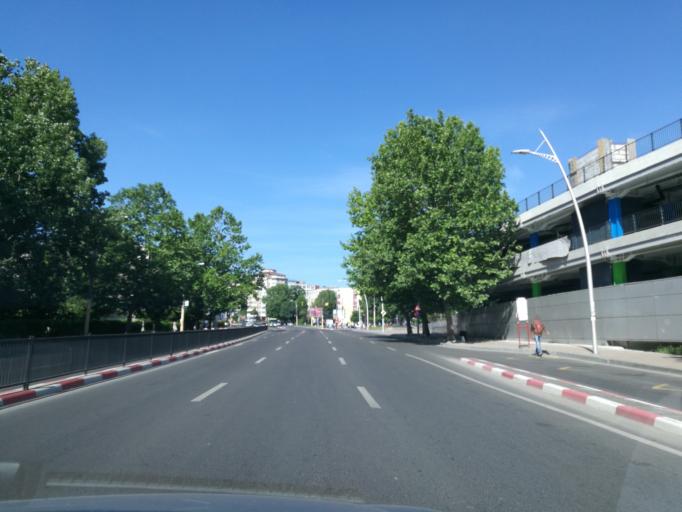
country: RO
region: Constanta
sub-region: Municipiul Constanta
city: Constanta
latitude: 44.2026
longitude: 28.6322
